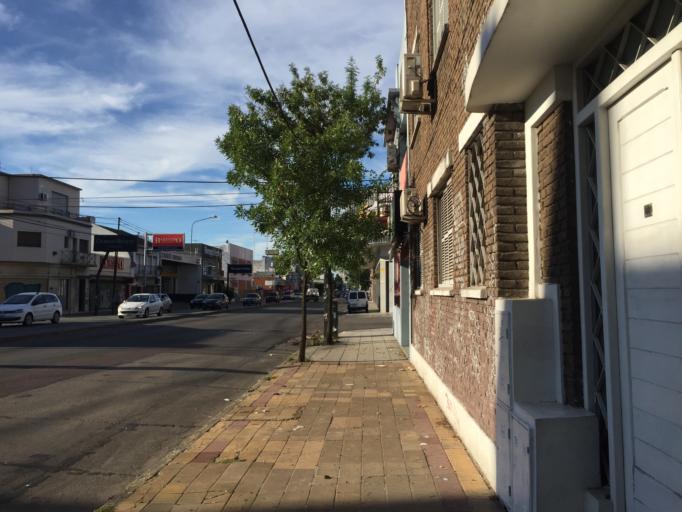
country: AR
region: Buenos Aires
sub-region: Partido de Lomas de Zamora
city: Lomas de Zamora
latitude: -34.7417
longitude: -58.3986
